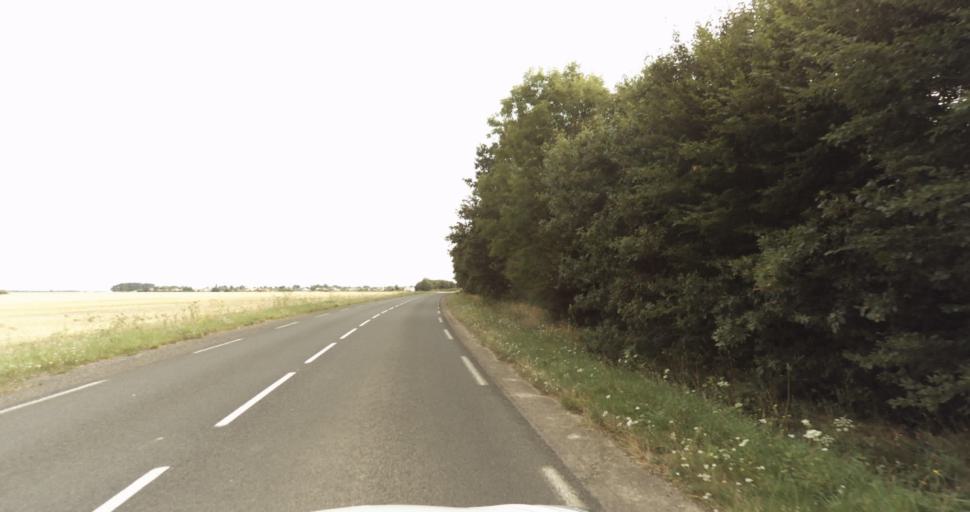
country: FR
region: Haute-Normandie
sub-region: Departement de l'Eure
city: La Madeleine-de-Nonancourt
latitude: 48.8493
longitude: 1.2417
